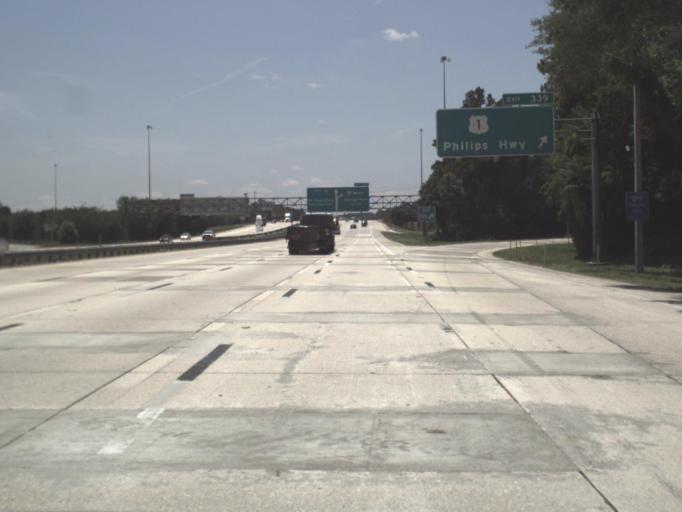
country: US
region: Florida
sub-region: Saint Johns County
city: Fruit Cove
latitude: 30.1889
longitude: -81.5576
